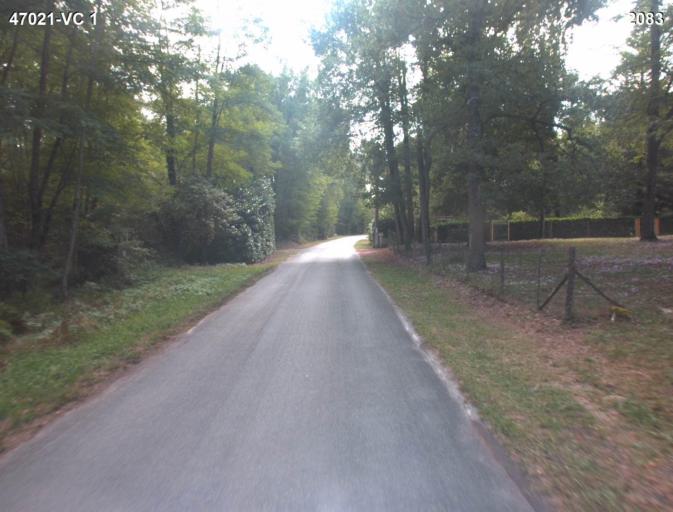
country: FR
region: Aquitaine
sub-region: Departement du Lot-et-Garonne
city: Barbaste
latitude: 44.1490
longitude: 0.2941
